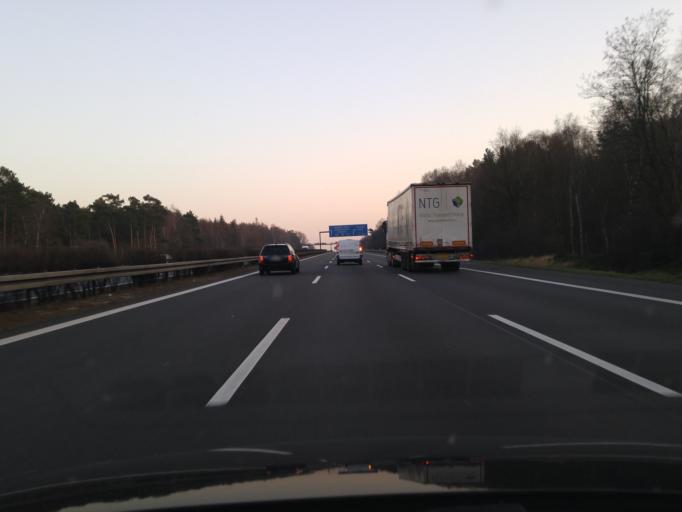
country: DE
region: Brandenburg
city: Fichtenwalde
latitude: 52.3006
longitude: 12.8955
